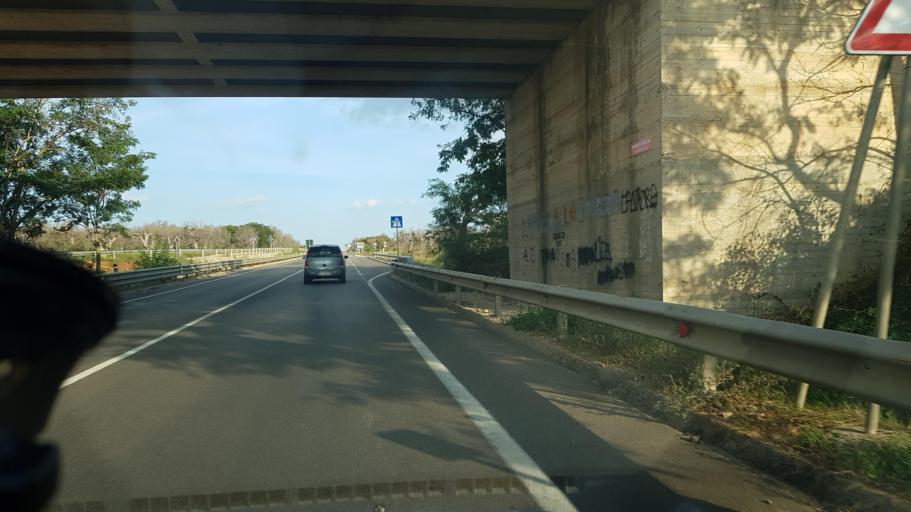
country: IT
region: Apulia
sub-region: Provincia di Lecce
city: Acquarica del Capo
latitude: 39.9179
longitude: 18.2177
